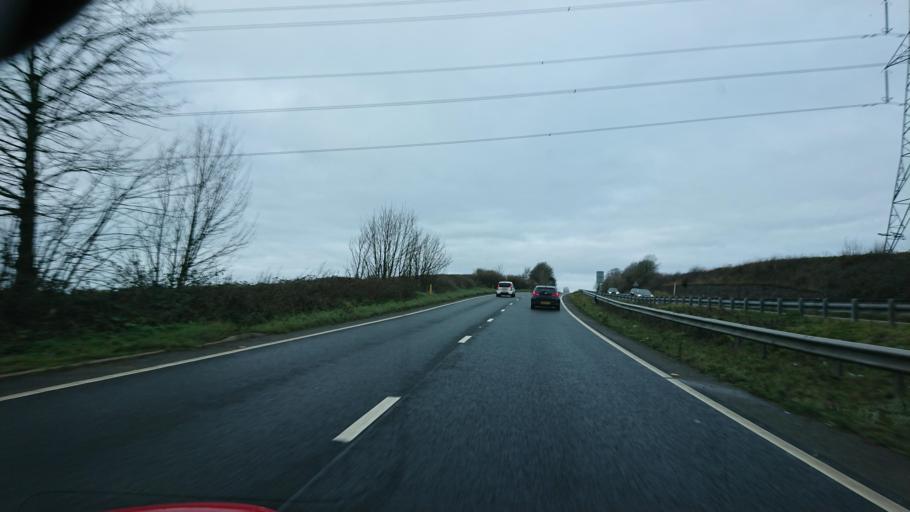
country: GB
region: England
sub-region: Cornwall
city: Liskeard
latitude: 50.4363
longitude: -4.4403
